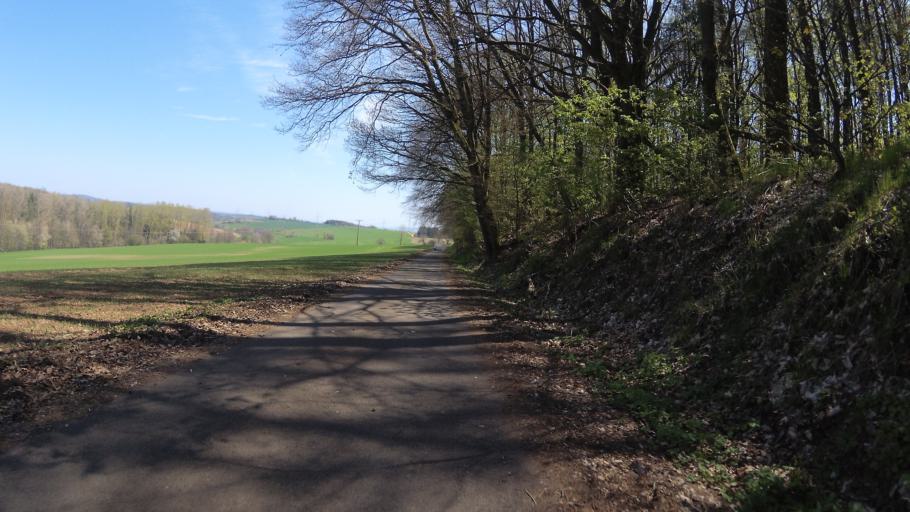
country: DE
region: Rheinland-Pfalz
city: Waldmohr
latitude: 49.3985
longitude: 7.3208
